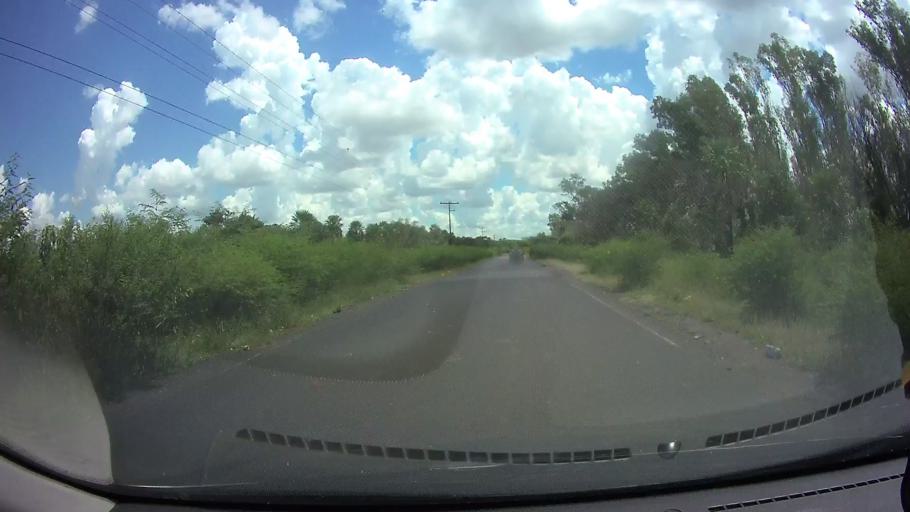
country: PY
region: Presidente Hayes
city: Nanawa
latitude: -25.2457
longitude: -57.6722
